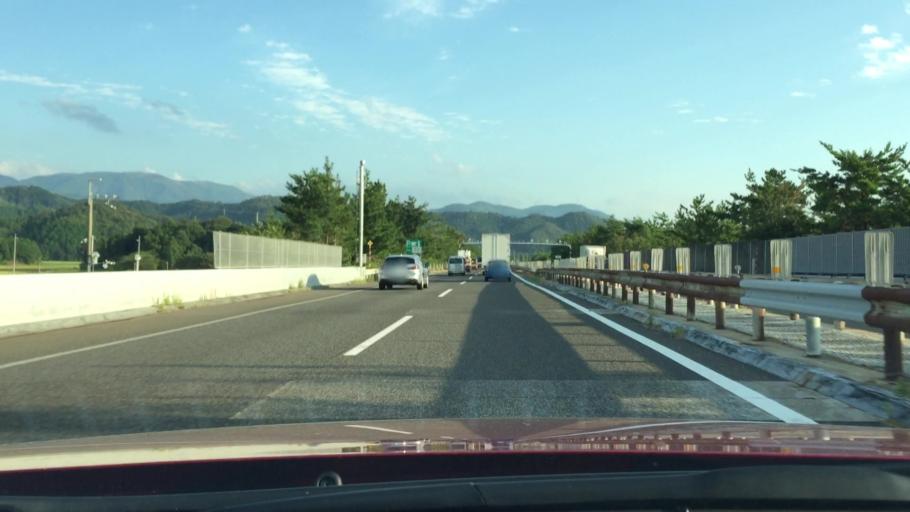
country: JP
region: Shiga Prefecture
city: Nagahama
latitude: 35.3681
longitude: 136.3051
